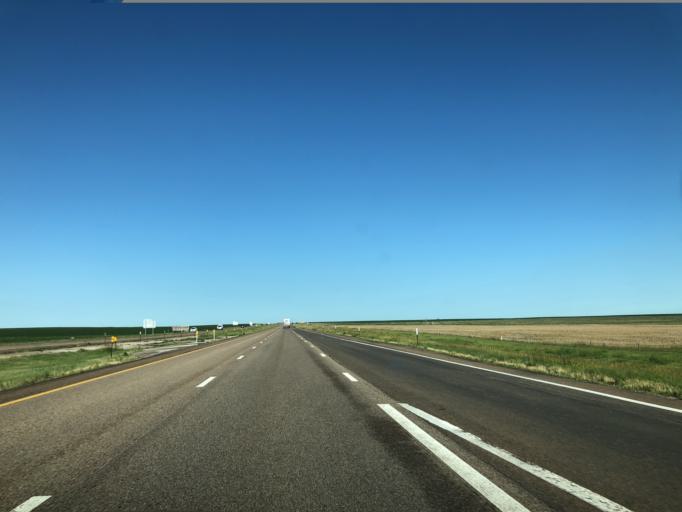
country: US
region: Kansas
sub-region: Thomas County
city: Colby
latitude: 39.3663
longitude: -101.2063
